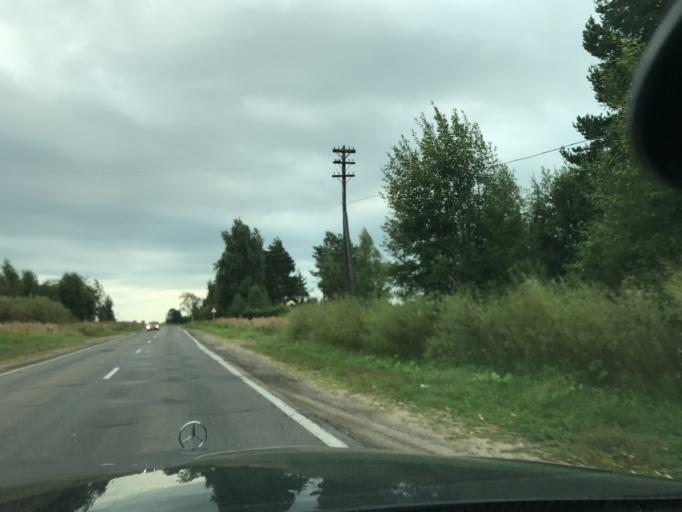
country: RU
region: Vladimir
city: Gorokhovets
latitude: 56.1888
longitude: 42.7590
